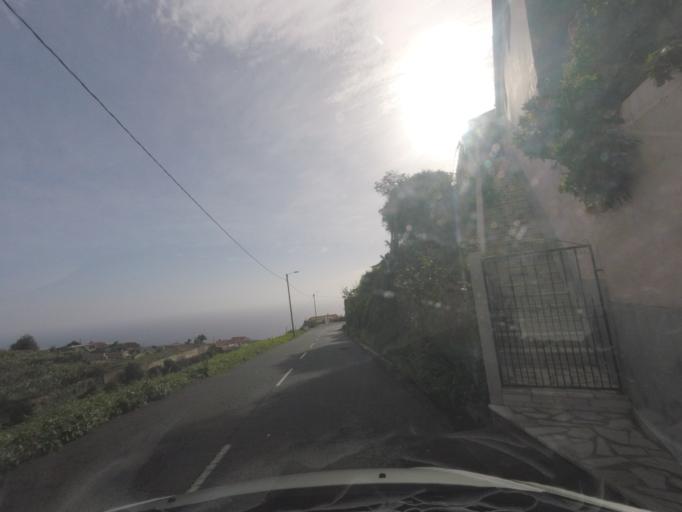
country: PT
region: Madeira
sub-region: Calheta
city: Estreito da Calheta
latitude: 32.7345
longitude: -17.1905
